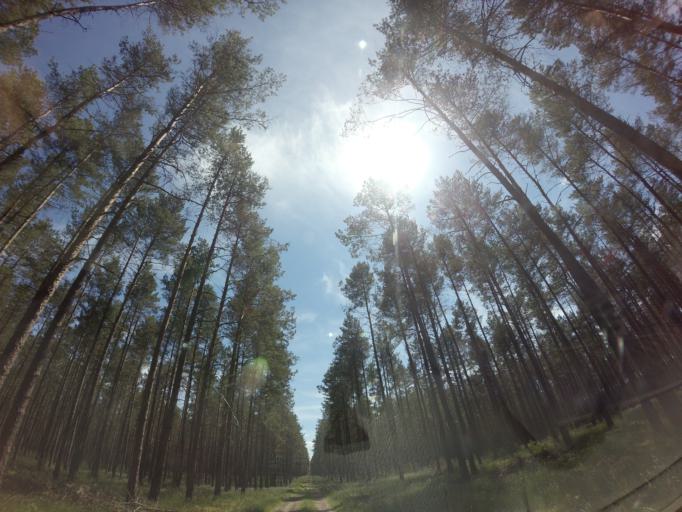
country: PL
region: West Pomeranian Voivodeship
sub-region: Powiat drawski
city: Kalisz Pomorski
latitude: 53.1843
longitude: 15.8993
